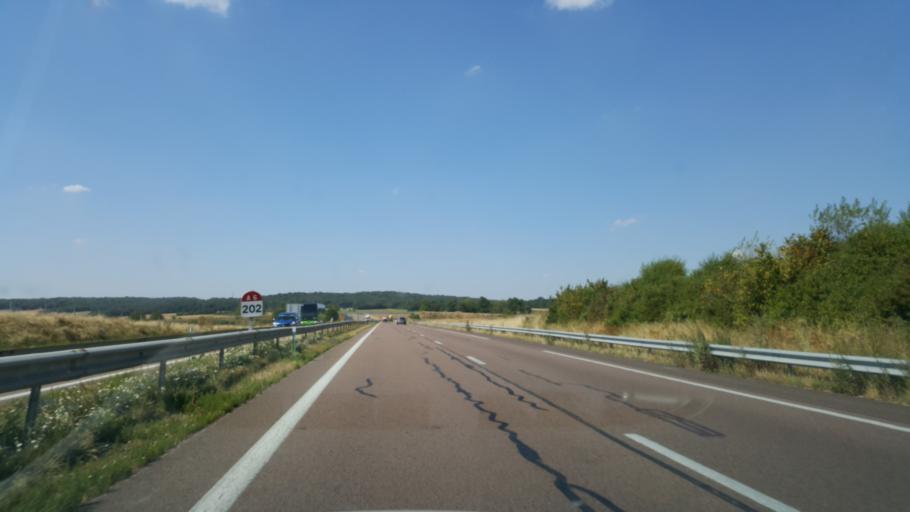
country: FR
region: Bourgogne
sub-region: Departement de l'Yonne
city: Avallon
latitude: 47.5674
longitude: 3.9401
